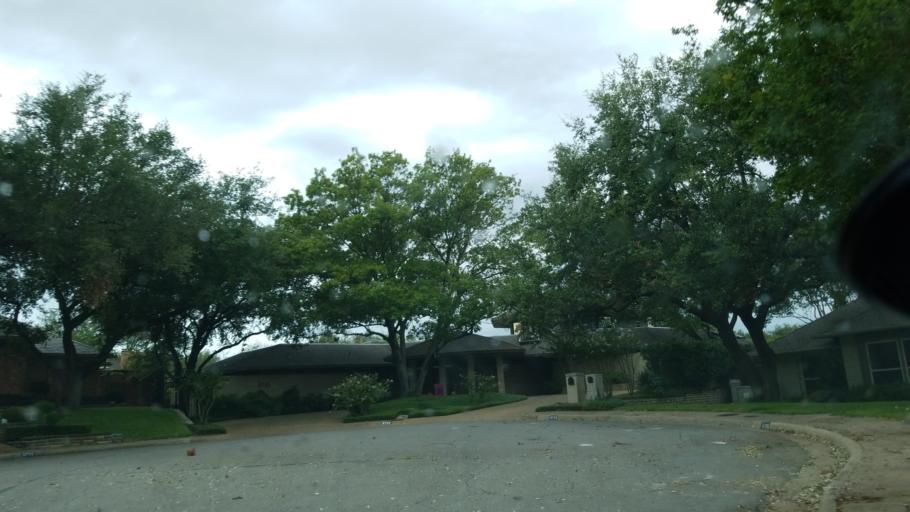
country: US
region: Texas
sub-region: Dallas County
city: Richardson
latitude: 32.8986
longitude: -96.7368
